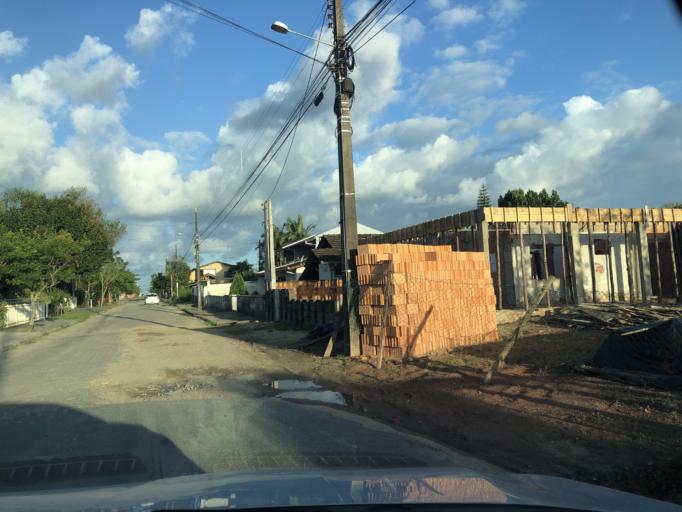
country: BR
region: Santa Catarina
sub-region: Sao Francisco Do Sul
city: Sao Francisco do Sul
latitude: -26.2166
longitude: -48.5302
